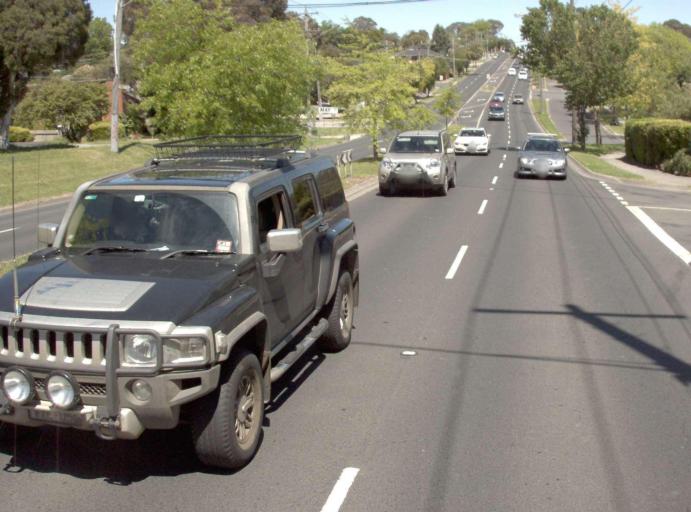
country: AU
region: Victoria
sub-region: Manningham
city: Donvale
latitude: -37.7842
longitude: 145.1628
